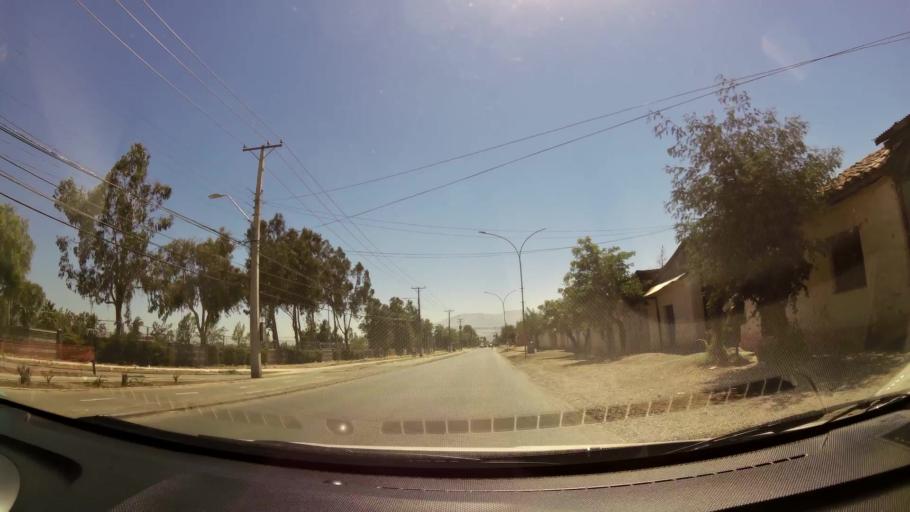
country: CL
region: O'Higgins
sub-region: Provincia de Cachapoal
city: Rancagua
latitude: -34.1634
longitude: -70.7134
